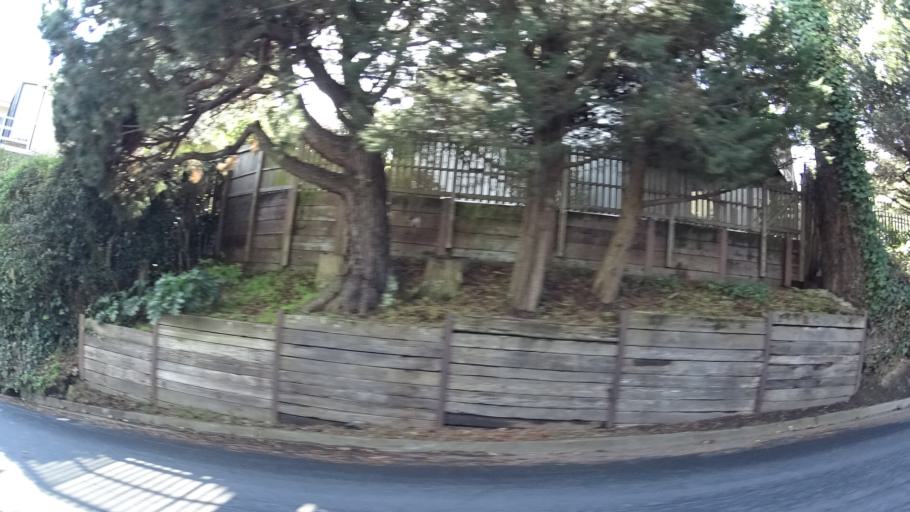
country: US
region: California
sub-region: San Mateo County
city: Millbrae
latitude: 37.5881
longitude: -122.4084
